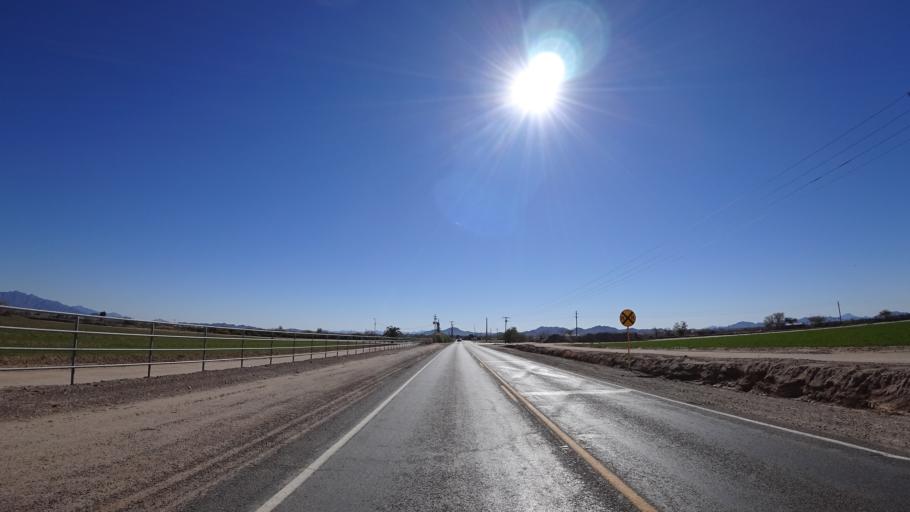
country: US
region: Arizona
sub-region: Maricopa County
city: Buckeye
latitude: 33.3933
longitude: -112.5215
